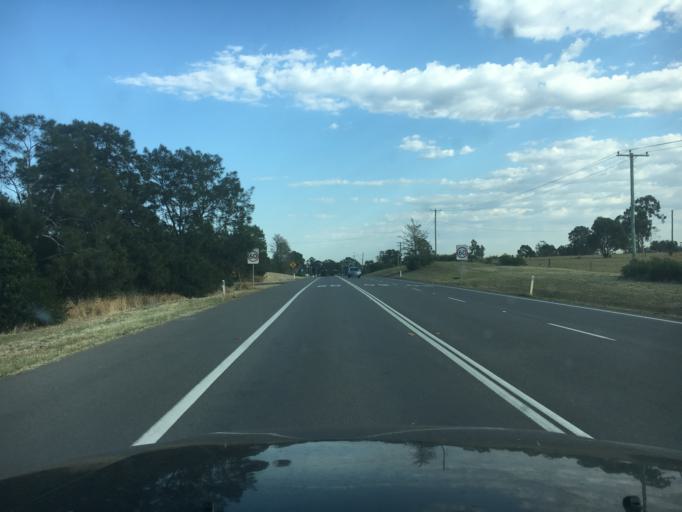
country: AU
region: New South Wales
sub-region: Cessnock
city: Branxton
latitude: -32.6601
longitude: 151.3649
